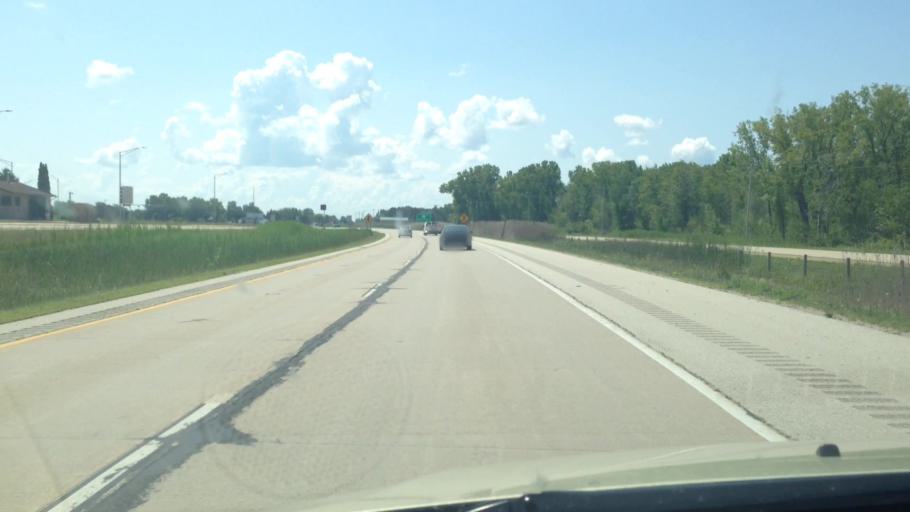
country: US
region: Wisconsin
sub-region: Brown County
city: Suamico
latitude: 44.7431
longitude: -88.0525
